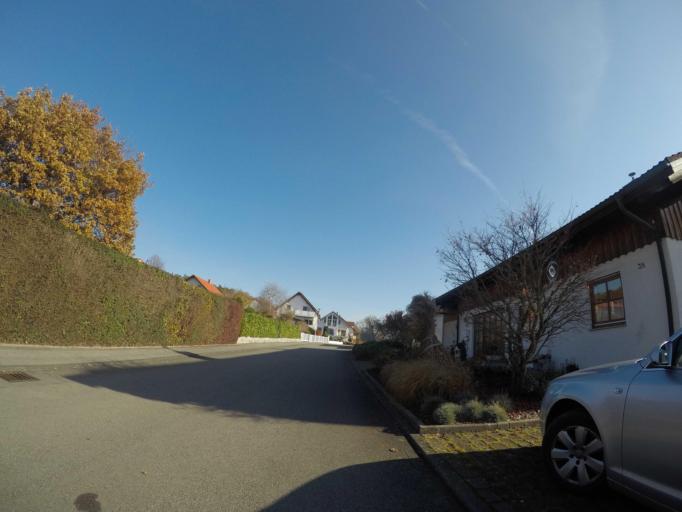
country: DE
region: Baden-Wuerttemberg
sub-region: Tuebingen Region
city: Rechtenstein
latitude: 48.2412
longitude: 9.5575
